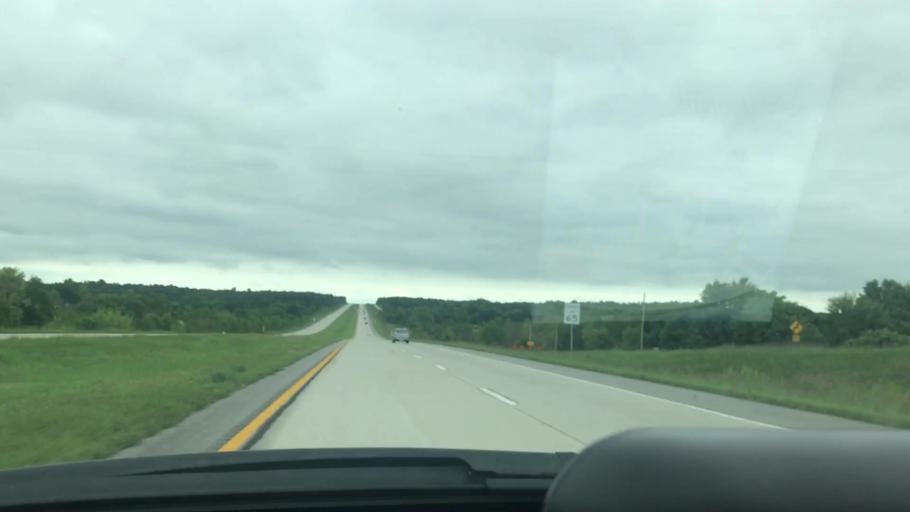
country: US
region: Missouri
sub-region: Greene County
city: Fair Grove
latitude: 37.4631
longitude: -93.1392
